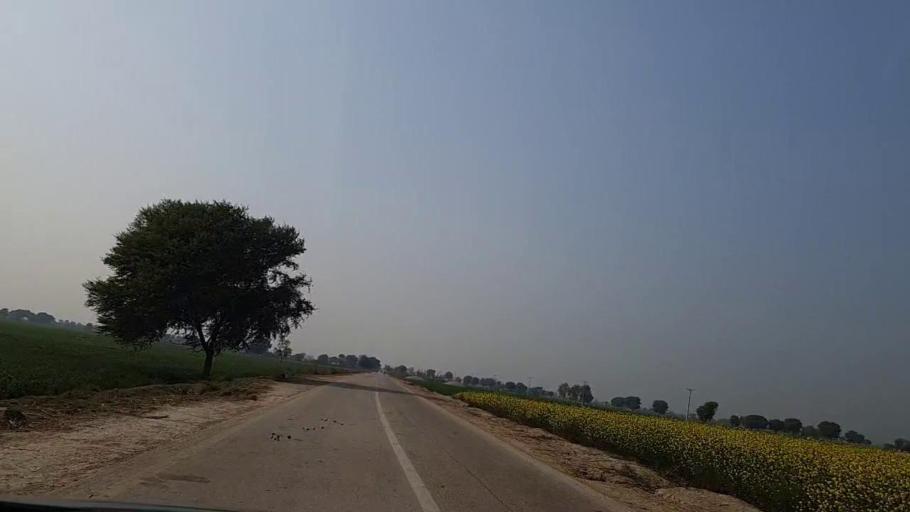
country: PK
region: Sindh
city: Sann
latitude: 26.1406
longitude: 68.1585
